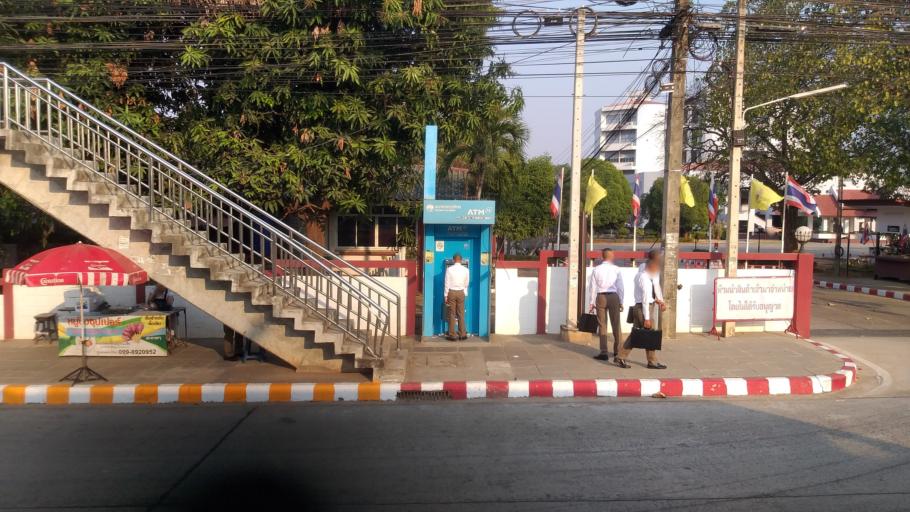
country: TH
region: Khon Kaen
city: Khon Kaen
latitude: 16.4809
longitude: 102.8328
